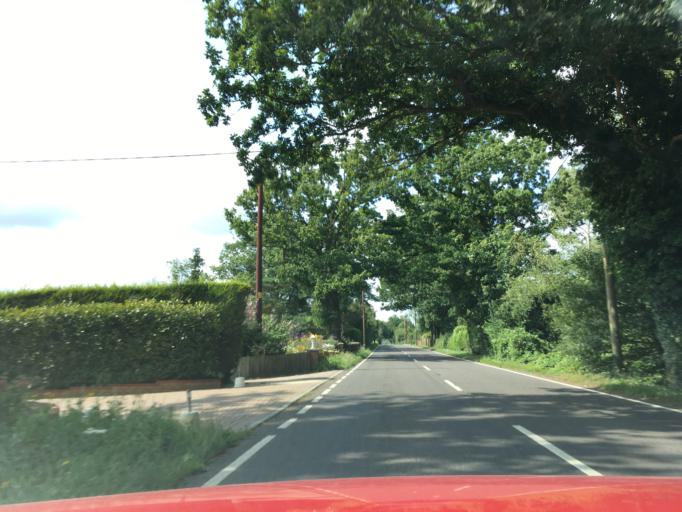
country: GB
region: England
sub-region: Kent
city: Headcorn
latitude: 51.1924
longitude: 0.6019
